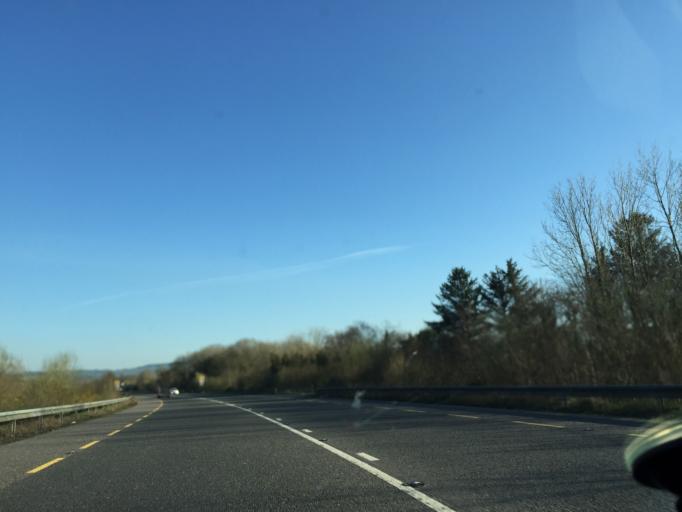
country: IE
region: Munster
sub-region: Ciarrai
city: Castleisland
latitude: 52.1967
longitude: -9.5702
